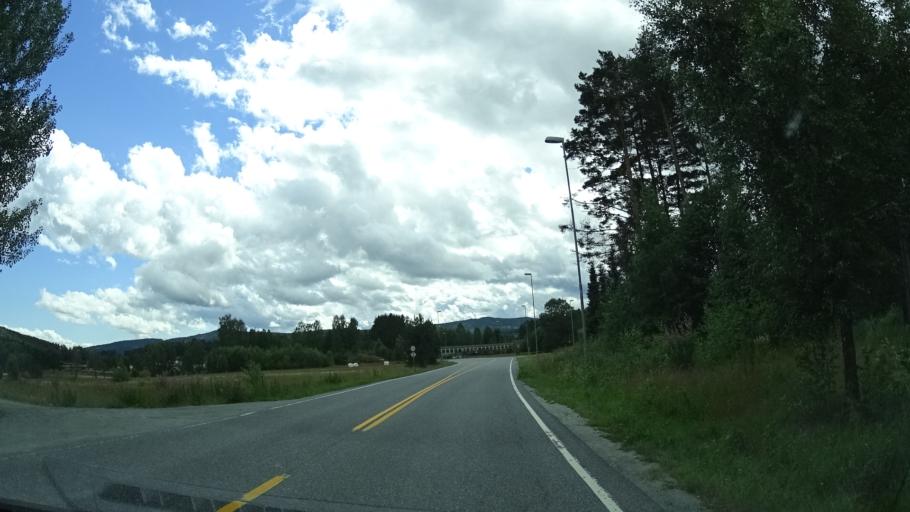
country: NO
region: Buskerud
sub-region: Krodsherad
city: Noresund
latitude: 60.1885
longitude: 9.6127
